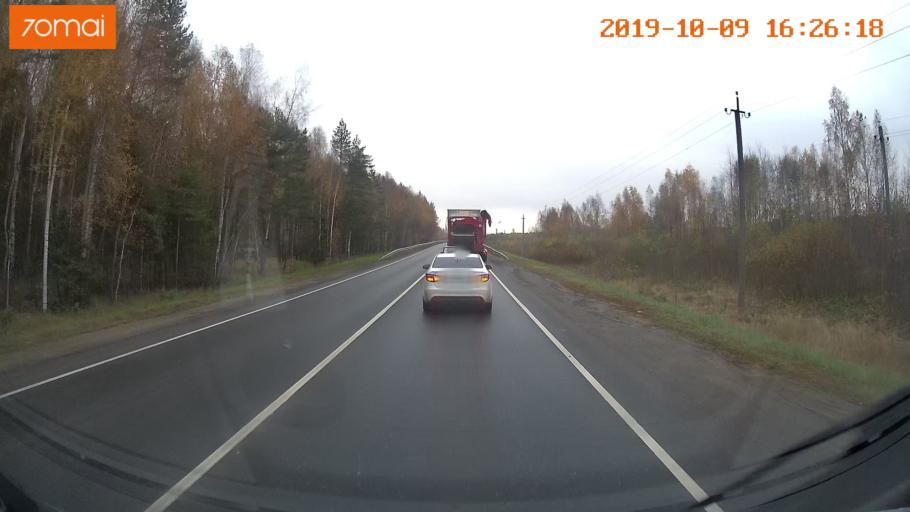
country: RU
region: Kostroma
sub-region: Kostromskoy Rayon
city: Kostroma
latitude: 57.6382
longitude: 40.9235
